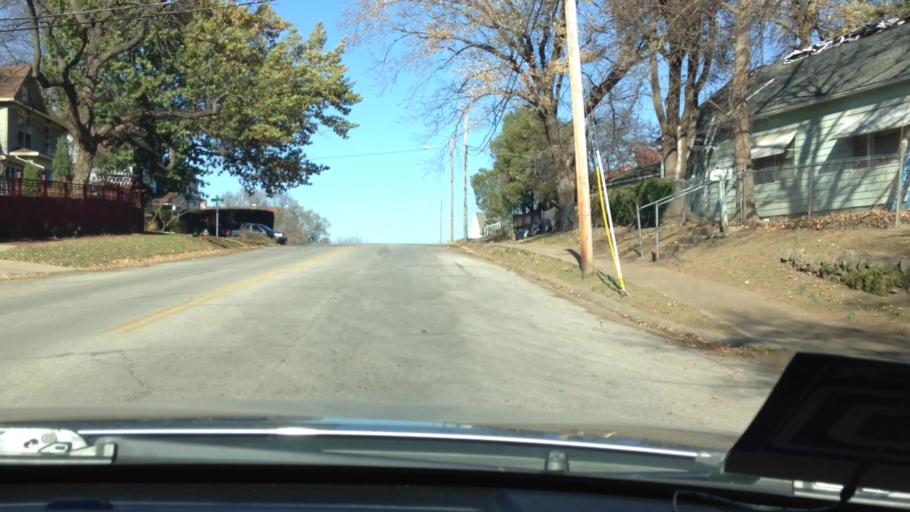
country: US
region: Kansas
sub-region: Leavenworth County
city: Leavenworth
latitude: 39.3069
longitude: -94.9136
